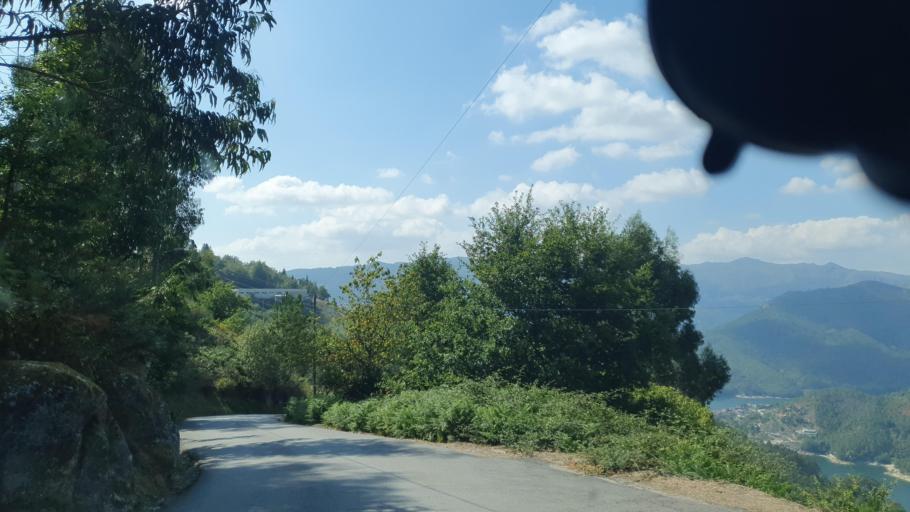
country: PT
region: Braga
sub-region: Vieira do Minho
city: Vieira do Minho
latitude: 41.6724
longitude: -8.1530
